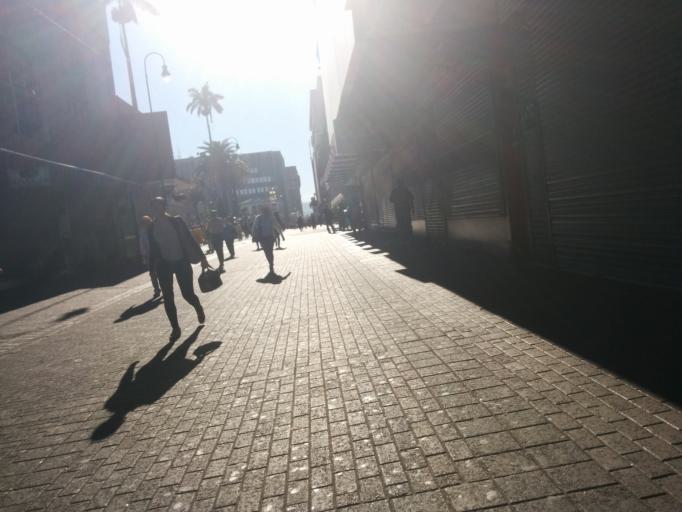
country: CR
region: San Jose
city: San Jose
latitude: 9.9324
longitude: -84.0804
